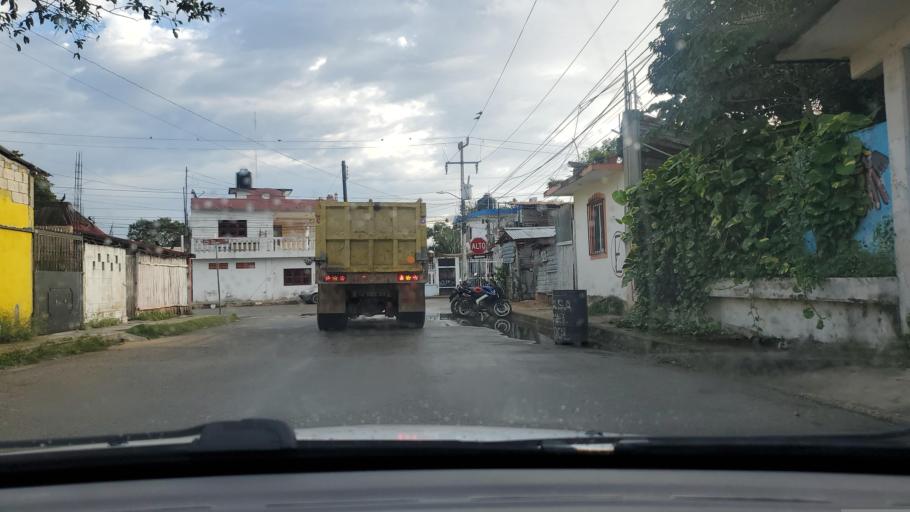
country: MX
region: Quintana Roo
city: Tulum
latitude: 20.2100
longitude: -87.4689
